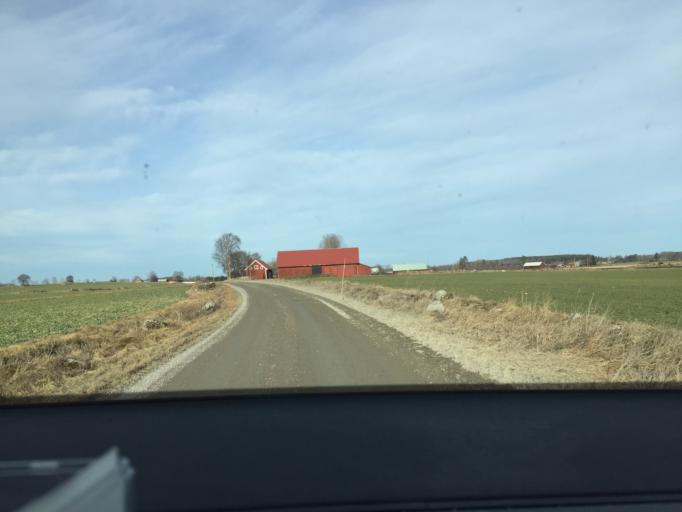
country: SE
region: OErebro
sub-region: Hallsbergs Kommun
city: Skollersta
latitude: 59.1297
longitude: 15.4300
